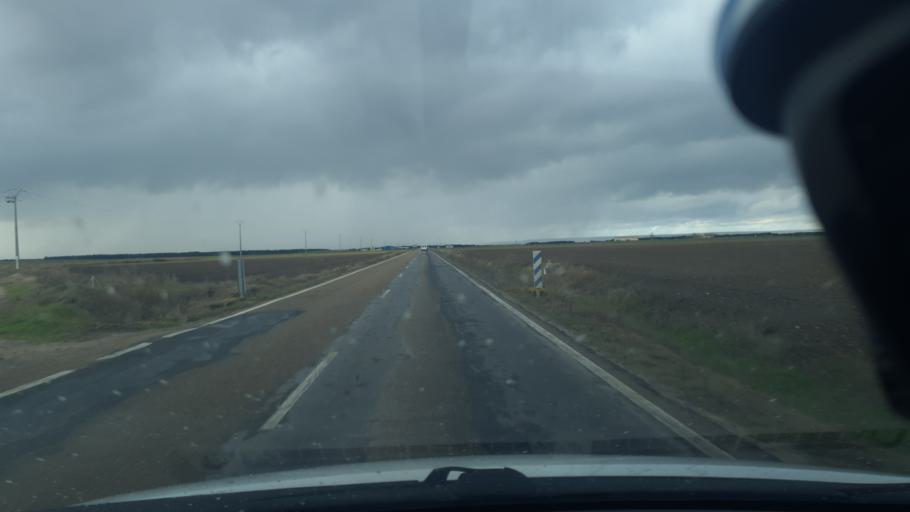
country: ES
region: Castille and Leon
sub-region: Provincia de Segovia
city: Chane
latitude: 41.3128
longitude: -4.3727
